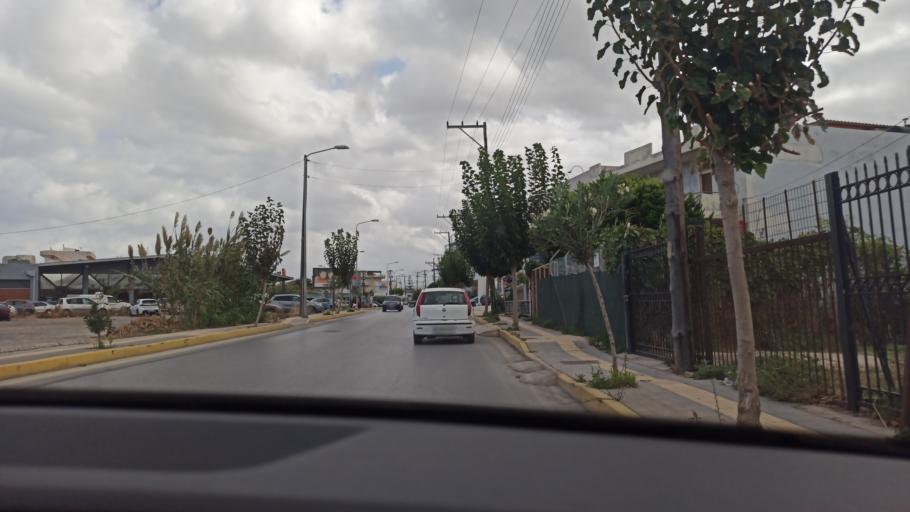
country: GR
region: Crete
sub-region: Nomos Irakleiou
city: Gazi
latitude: 35.3344
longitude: 25.0940
